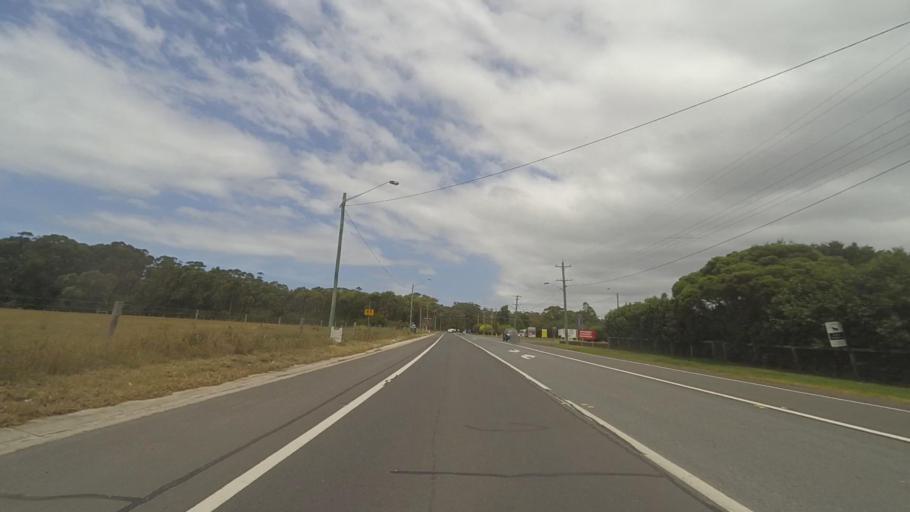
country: AU
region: New South Wales
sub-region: Shoalhaven Shire
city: Falls Creek
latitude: -35.0929
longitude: 150.5071
